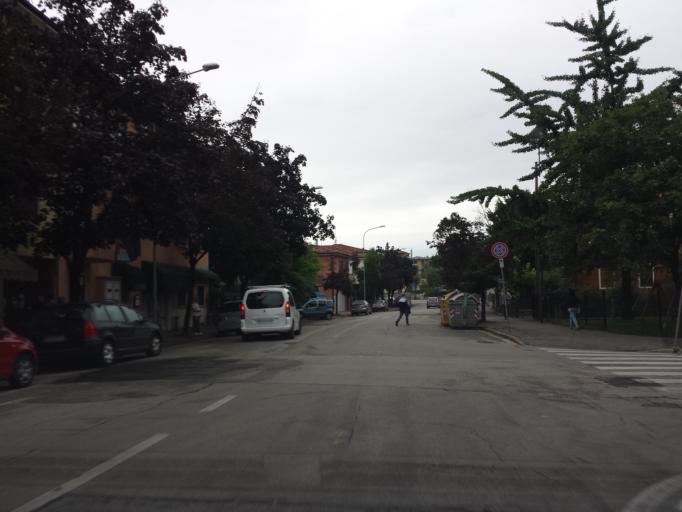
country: IT
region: Veneto
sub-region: Provincia di Vicenza
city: Vicenza
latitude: 45.5446
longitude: 11.5673
